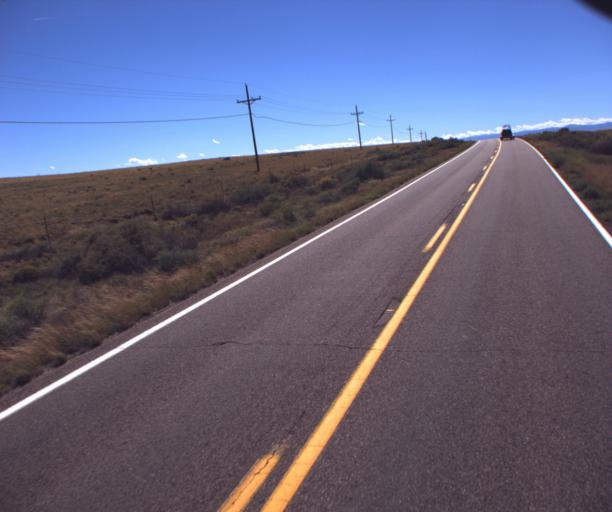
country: US
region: Arizona
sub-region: Apache County
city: Saint Johns
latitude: 34.5616
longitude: -109.3414
